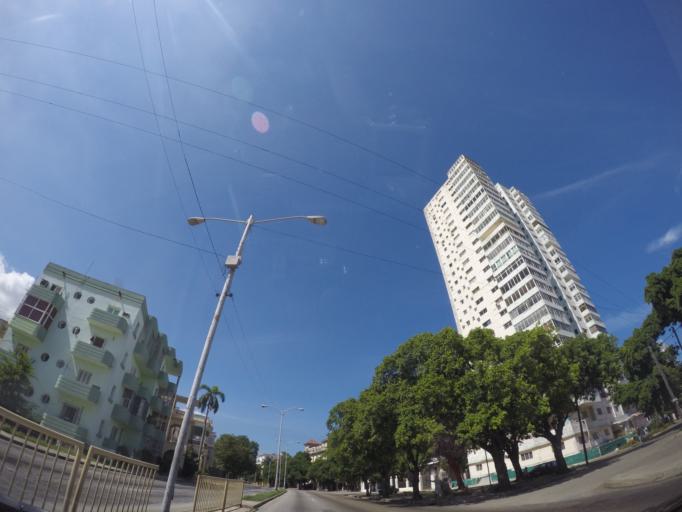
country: CU
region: La Habana
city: Regla
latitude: 23.1012
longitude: -82.3206
